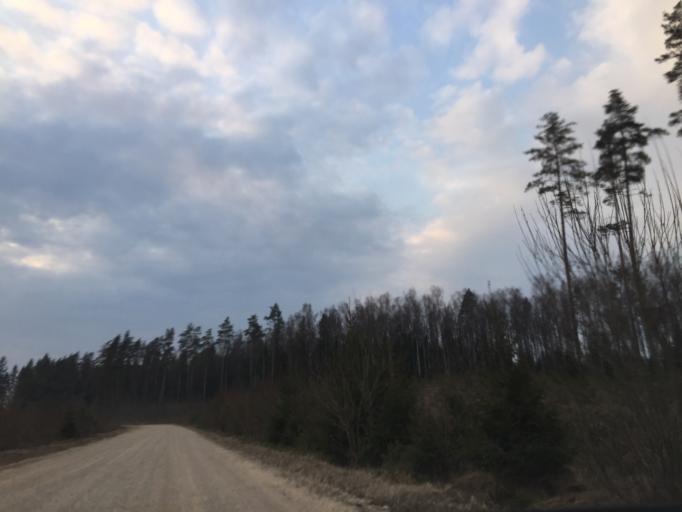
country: LV
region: Raunas
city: Rauna
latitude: 57.1364
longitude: 25.6314
